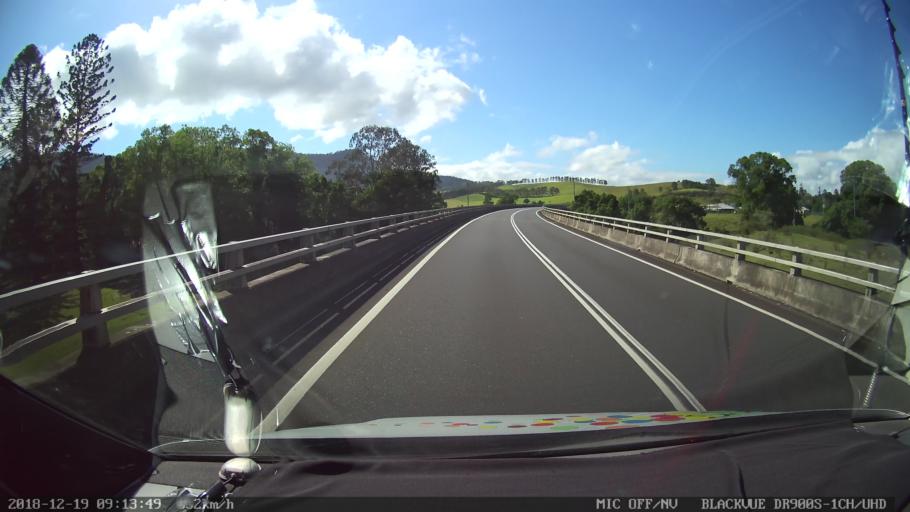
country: AU
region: New South Wales
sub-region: Kyogle
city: Kyogle
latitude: -28.5036
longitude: 152.9662
